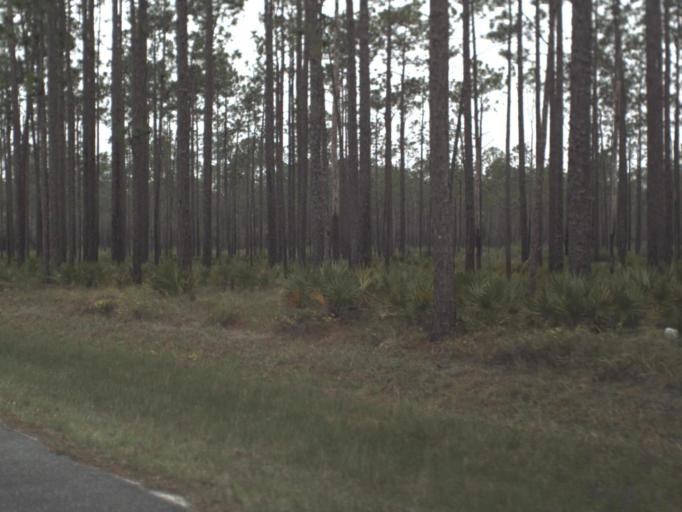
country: US
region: Florida
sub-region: Gulf County
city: Wewahitchka
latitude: 29.9852
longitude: -84.9760
